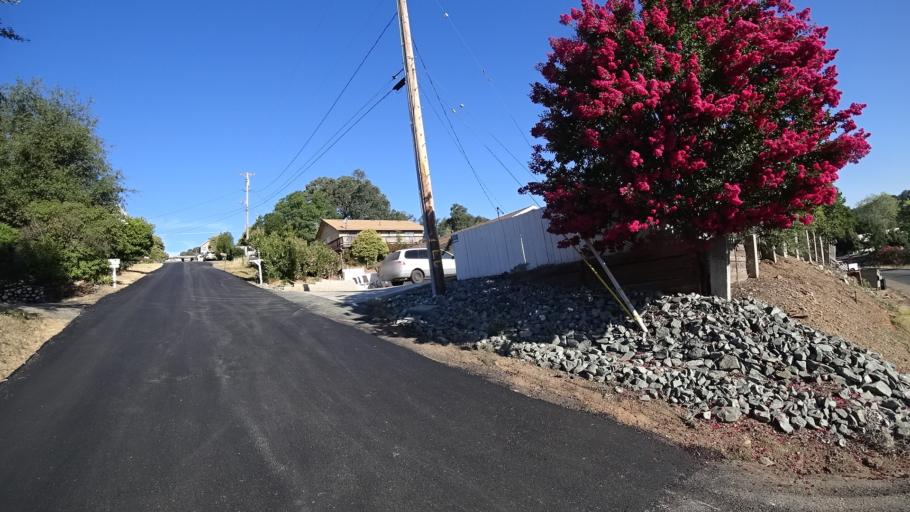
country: US
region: California
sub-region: Calaveras County
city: San Andreas
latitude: 38.1895
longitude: -120.6750
